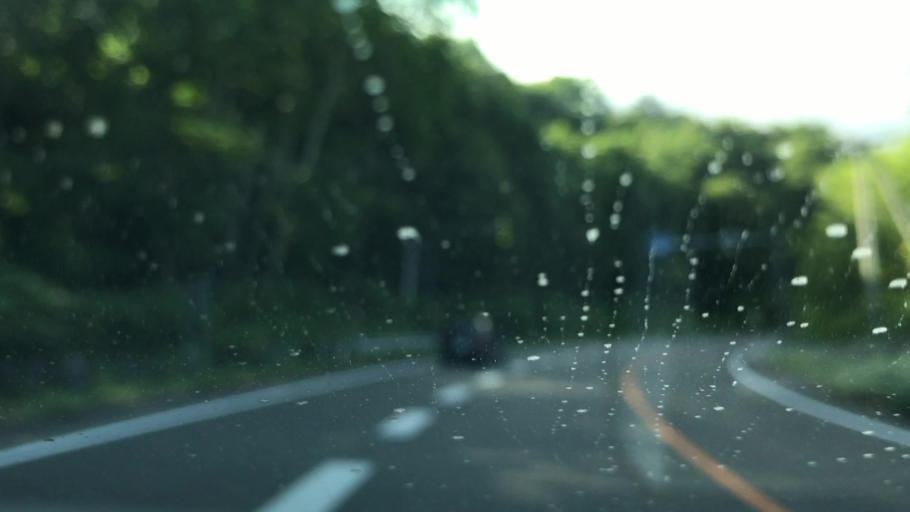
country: JP
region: Hokkaido
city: Shimo-furano
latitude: 42.9045
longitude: 142.4195
